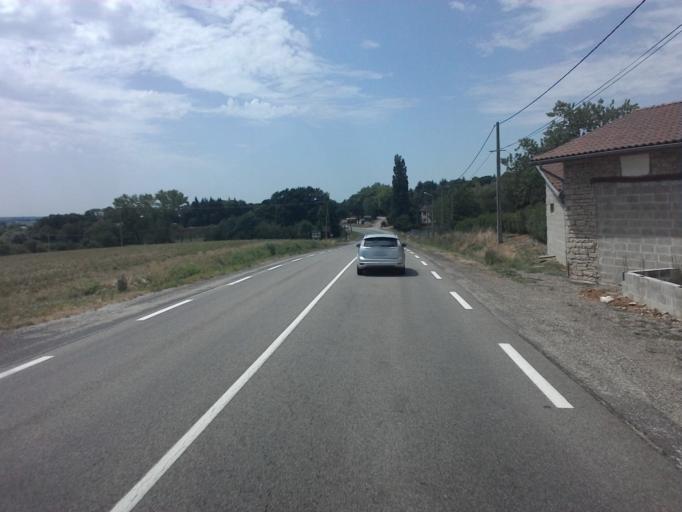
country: FR
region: Rhone-Alpes
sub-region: Departement de l'Ain
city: Coligny
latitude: 46.3643
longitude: 5.3326
